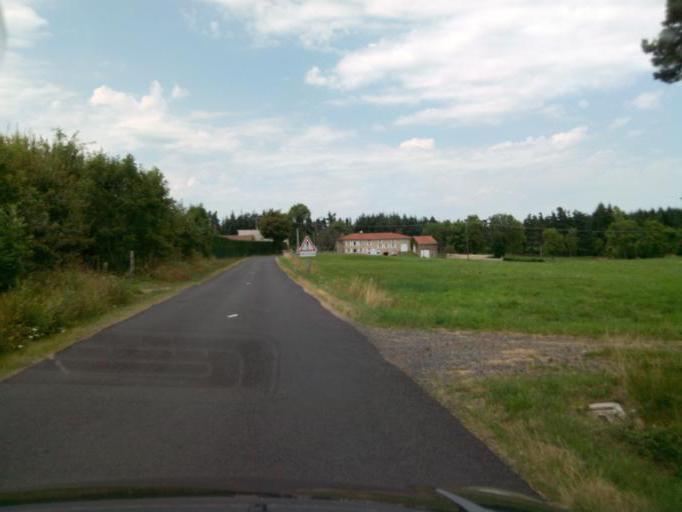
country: FR
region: Rhone-Alpes
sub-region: Departement de la Loire
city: Saint-Bonnet-le-Chateau
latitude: 45.3792
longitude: 4.0974
